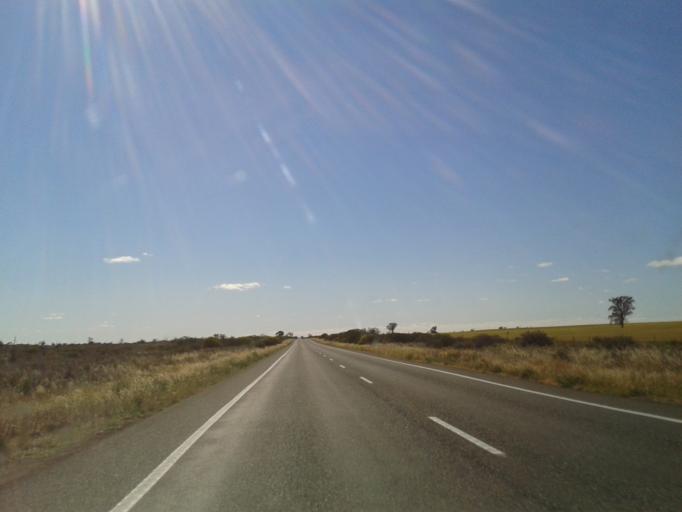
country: AU
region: South Australia
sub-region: Renmark Paringa
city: Renmark
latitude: -34.2750
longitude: 141.1489
